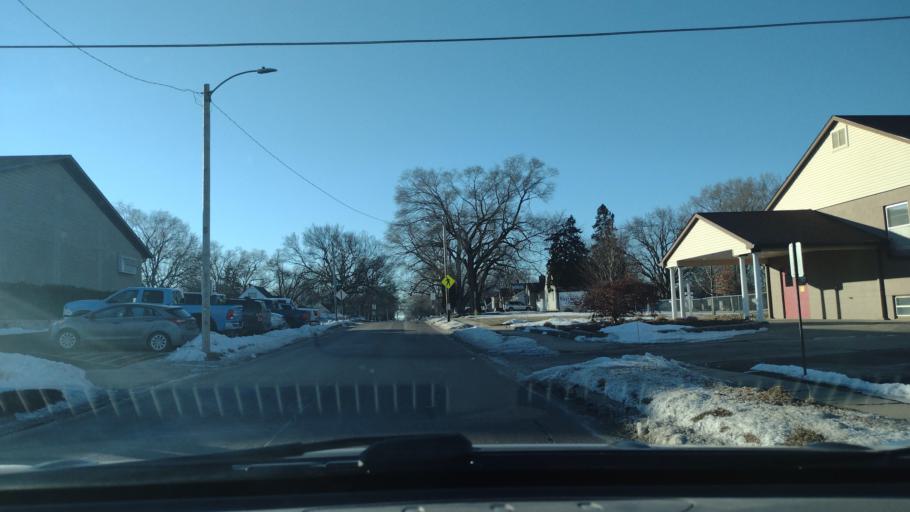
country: US
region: Nebraska
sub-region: Sarpy County
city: Bellevue
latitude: 41.1361
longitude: -95.8924
